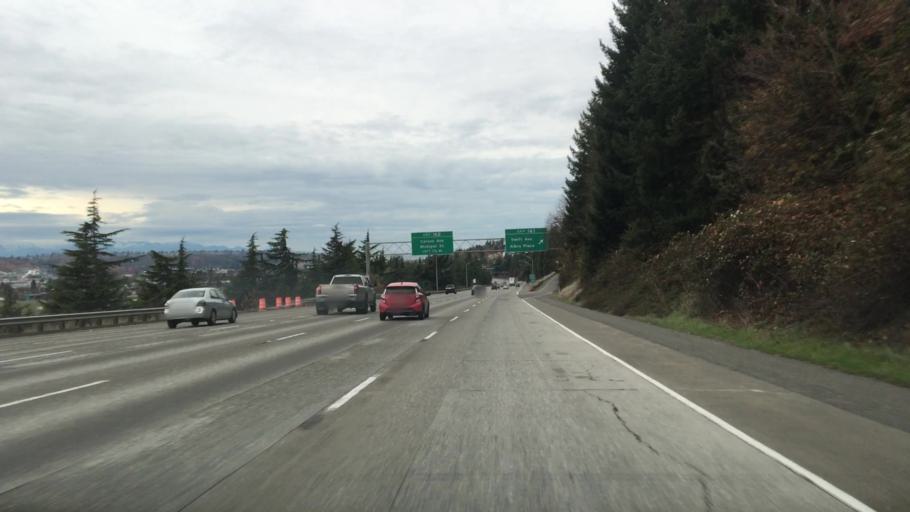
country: US
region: Washington
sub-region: King County
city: Boulevard Park
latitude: 47.5417
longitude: -122.3031
